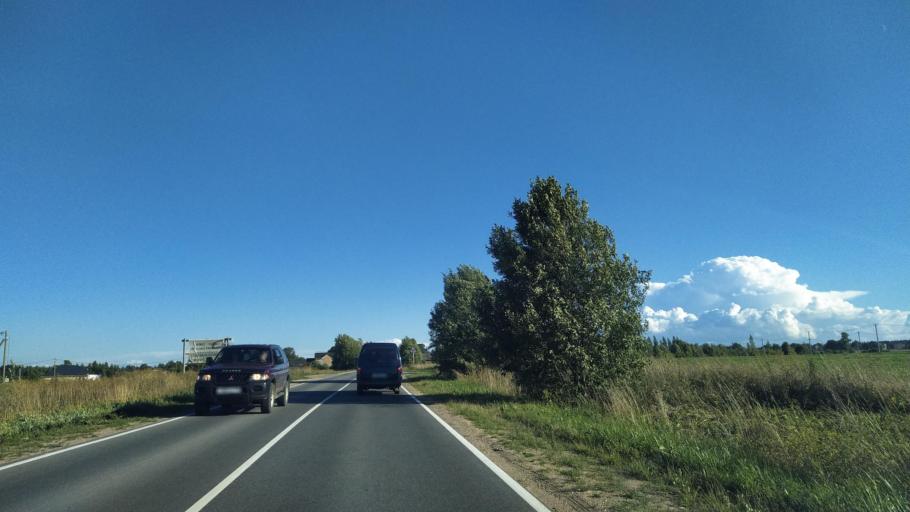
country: RU
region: Leningrad
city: Siverskiy
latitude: 59.3354
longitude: 30.0299
